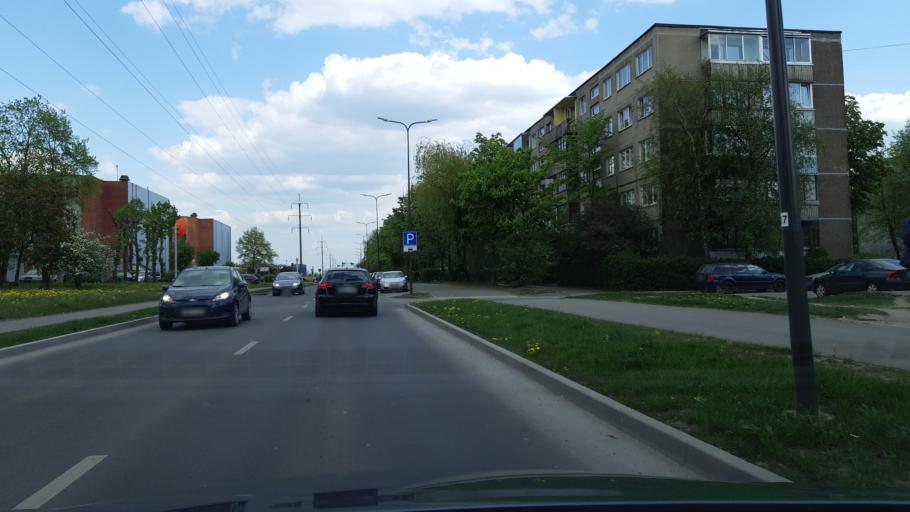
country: LT
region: Kauno apskritis
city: Dainava (Kaunas)
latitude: 54.9251
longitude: 23.9710
